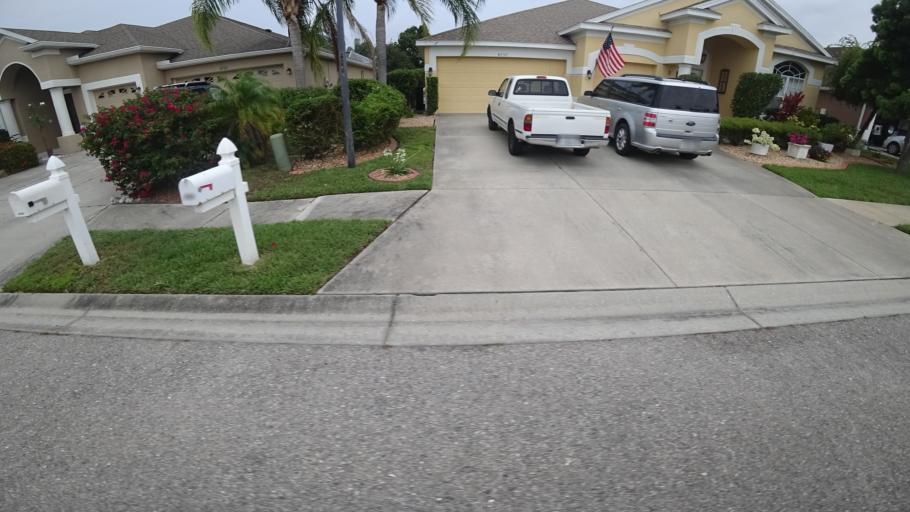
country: US
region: Florida
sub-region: Manatee County
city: Samoset
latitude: 27.4563
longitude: -82.4996
